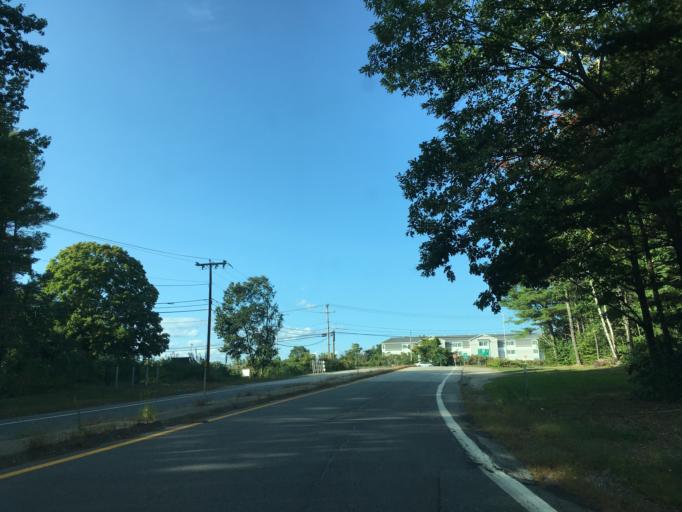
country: US
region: New Hampshire
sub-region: Rockingham County
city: Hampton
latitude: 42.9547
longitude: -70.8564
